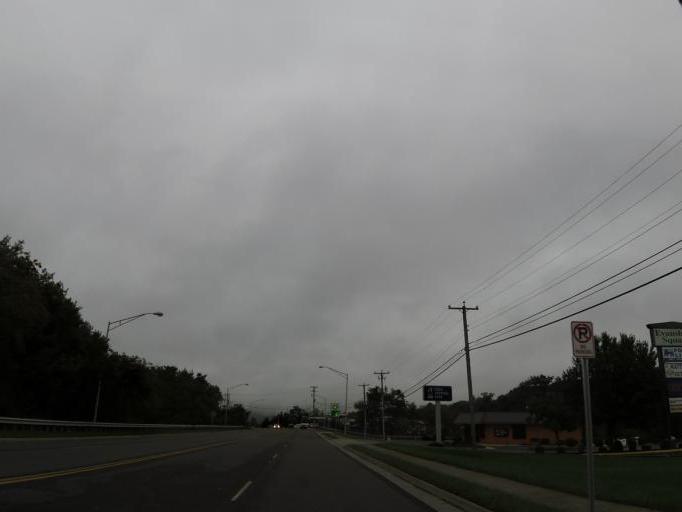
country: US
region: Virginia
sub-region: Wythe County
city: Wytheville
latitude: 36.9569
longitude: -81.0945
